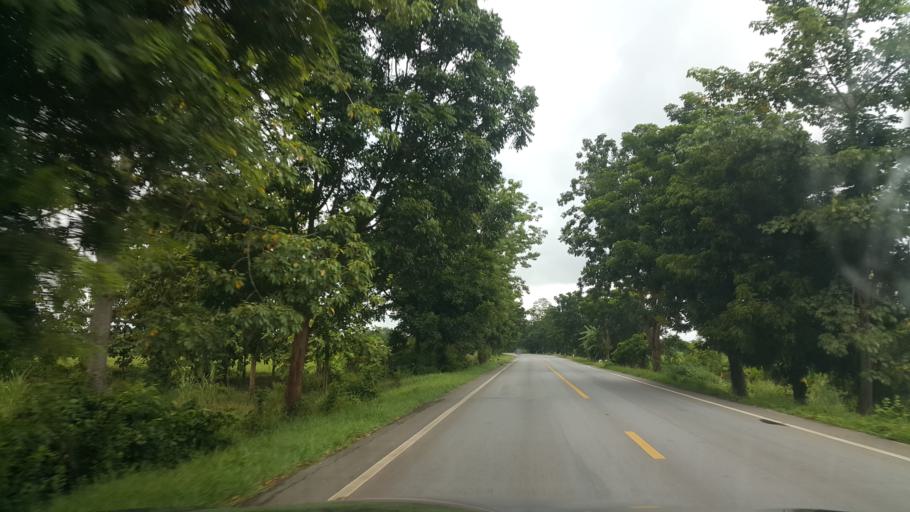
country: TH
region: Sukhothai
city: Sawankhalok
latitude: 17.3683
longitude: 99.7415
